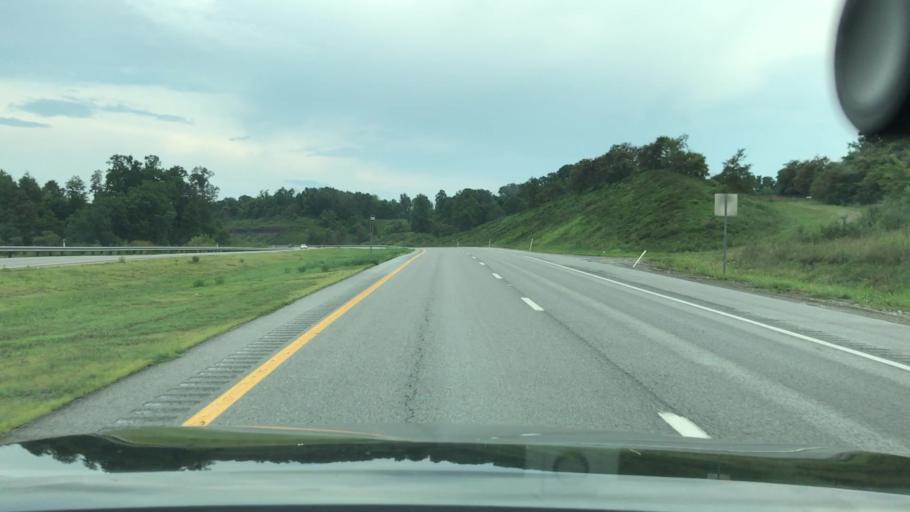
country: US
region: West Virginia
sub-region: Mason County
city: Point Pleasant
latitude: 38.7927
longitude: -82.0954
